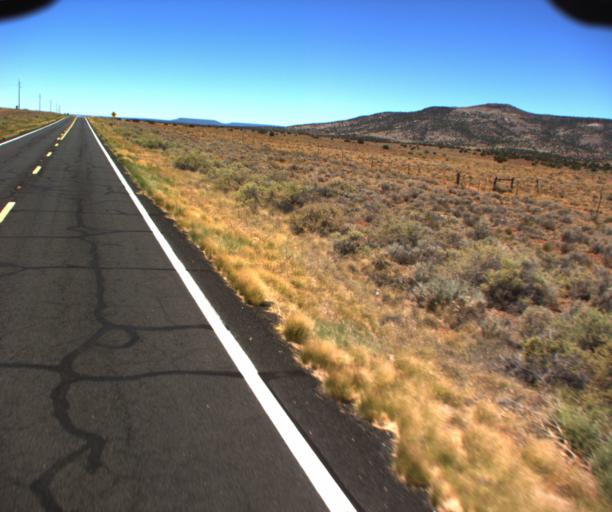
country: US
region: Arizona
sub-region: Coconino County
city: LeChee
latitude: 34.8752
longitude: -110.8939
